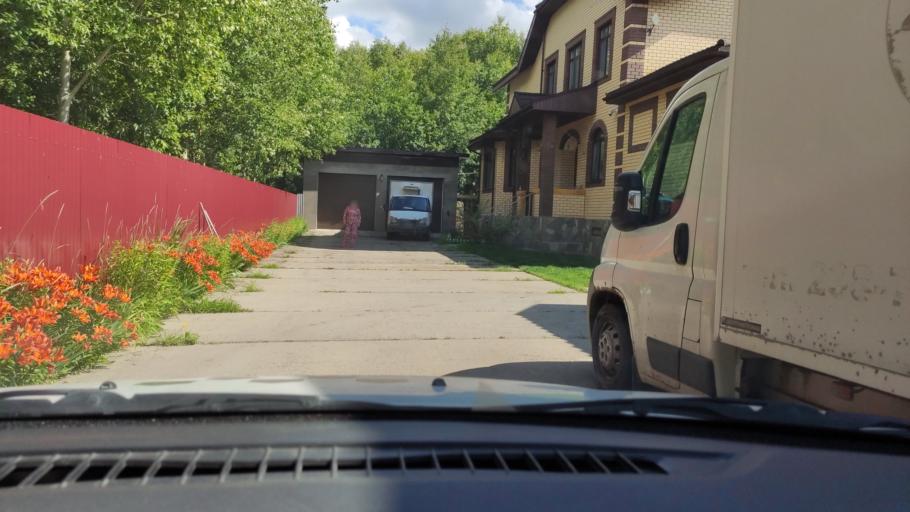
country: RU
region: Perm
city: Kondratovo
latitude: 57.9981
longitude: 56.0447
